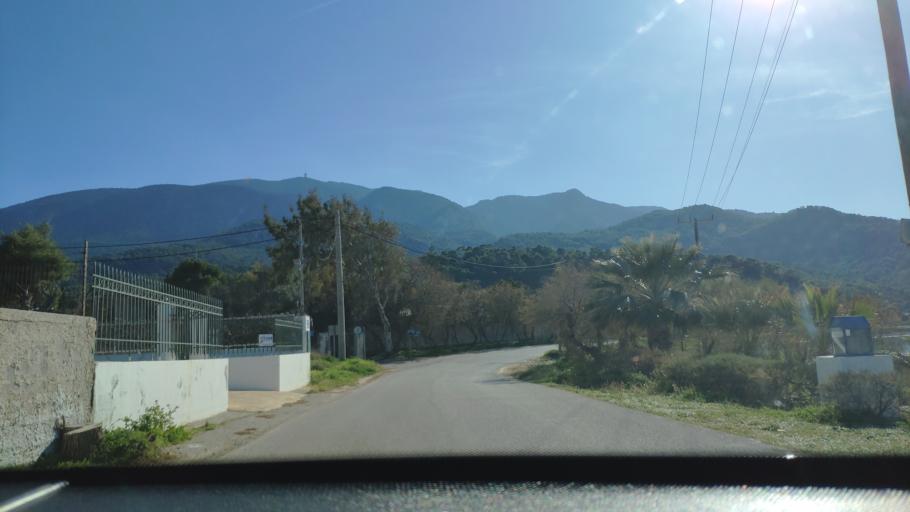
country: GR
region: Attica
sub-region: Nomarchia Dytikis Attikis
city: Kineta
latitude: 38.0689
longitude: 23.1500
